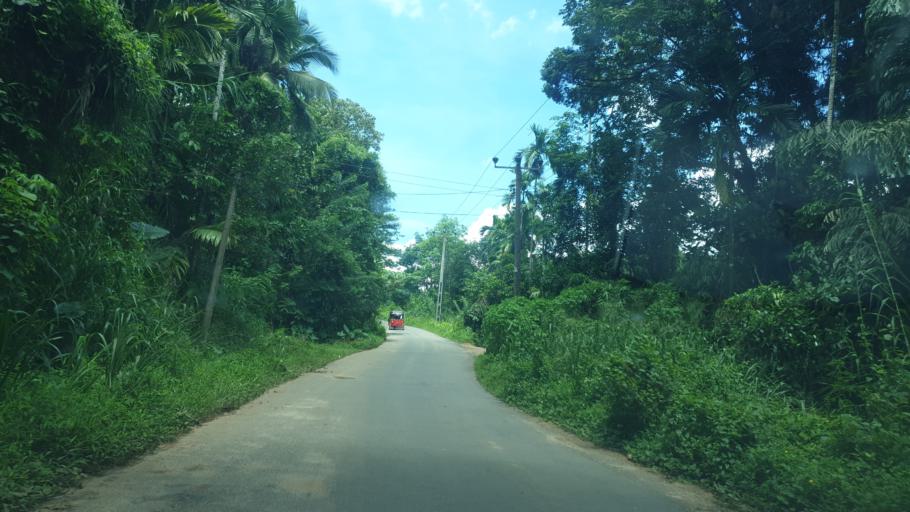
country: LK
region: Sabaragamuwa
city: Ratnapura
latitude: 6.4823
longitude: 80.4096
